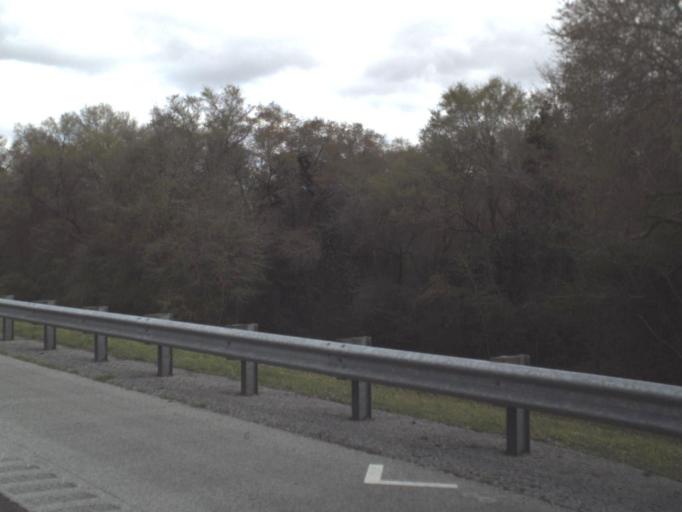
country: US
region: Florida
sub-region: Walton County
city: DeFuniak Springs
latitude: 30.7483
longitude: -86.2459
